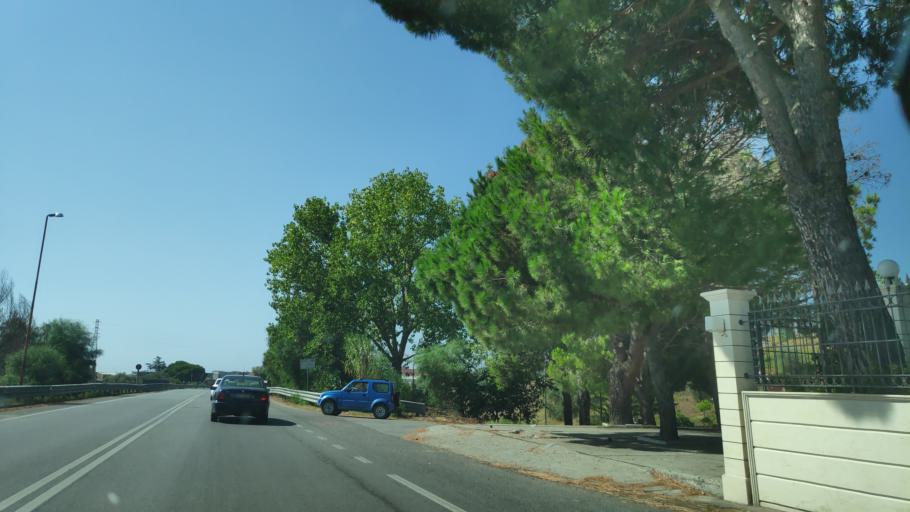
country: IT
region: Calabria
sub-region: Provincia di Reggio Calabria
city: Bovalino
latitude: 38.1469
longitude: 16.1679
